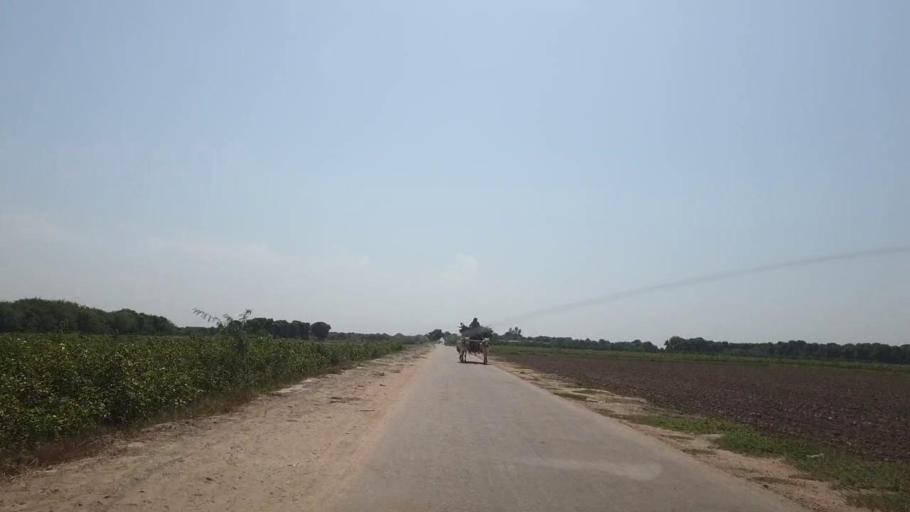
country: PK
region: Sindh
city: Tando Allahyar
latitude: 25.4048
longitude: 68.6439
